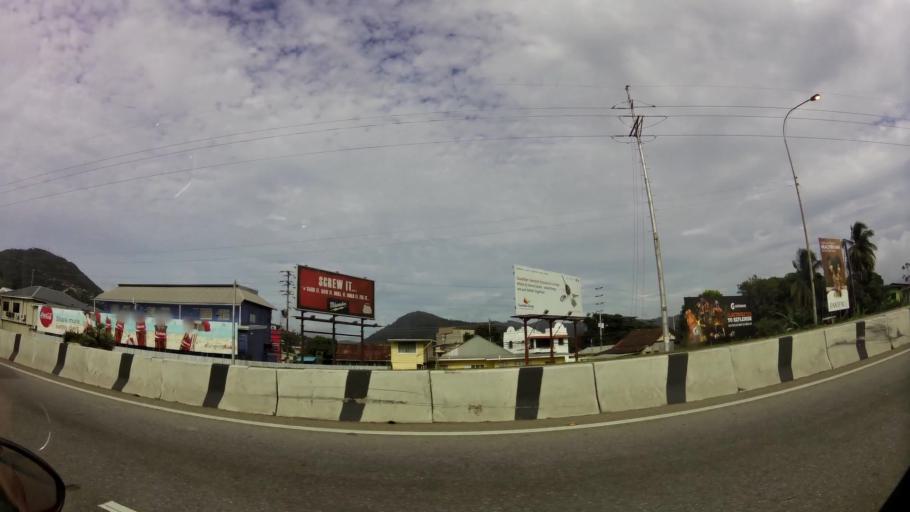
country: TT
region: City of Port of Spain
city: Mucurapo
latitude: 10.6683
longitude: -61.5369
